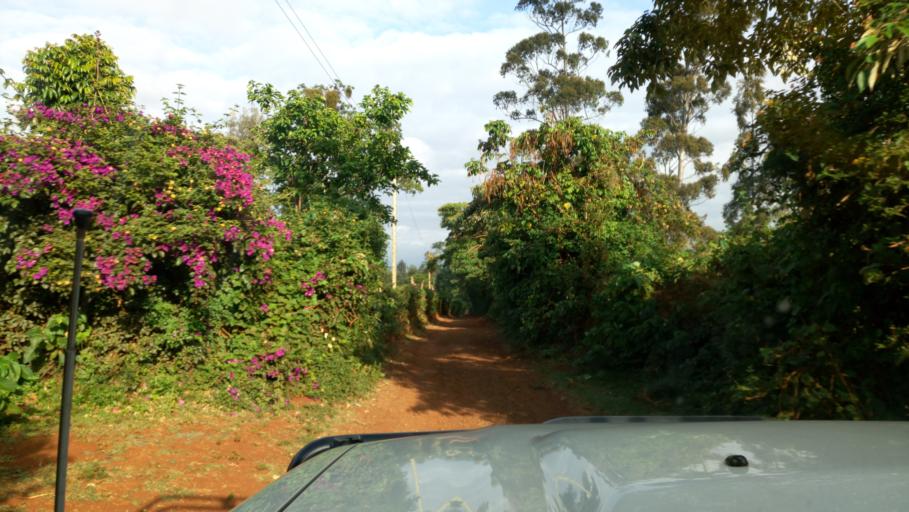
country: KE
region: Nyeri
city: Nyeri
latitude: -0.4474
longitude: 37.0561
